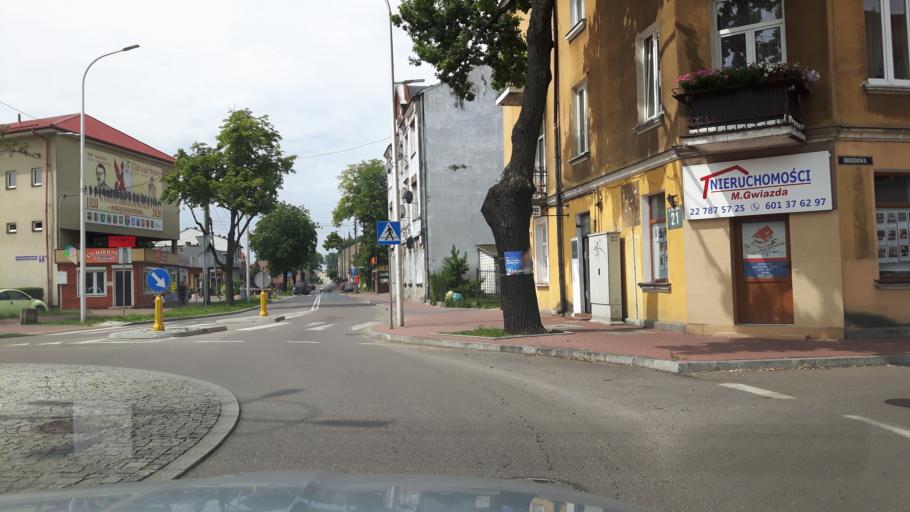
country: PL
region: Masovian Voivodeship
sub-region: Powiat wolominski
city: Wolomin
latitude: 52.3450
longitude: 21.2391
